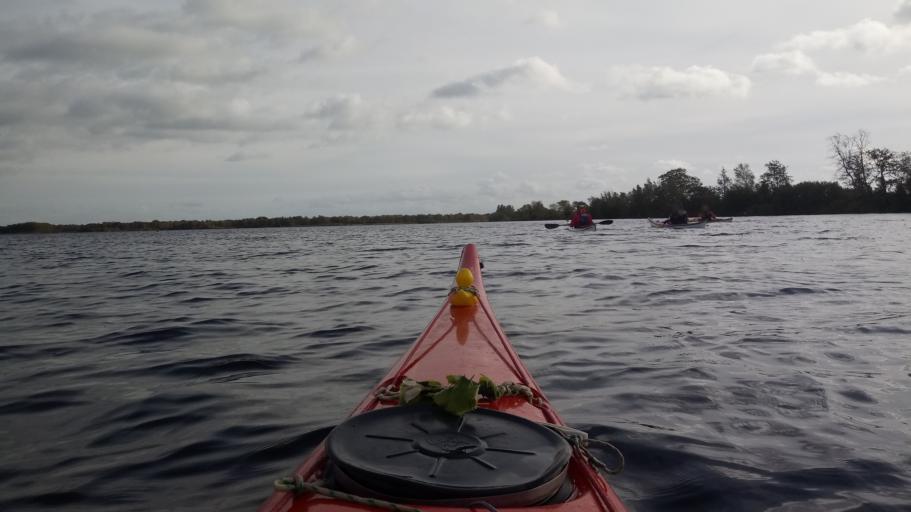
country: NL
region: Overijssel
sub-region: Gemeente Steenwijkerland
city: Wanneperveen
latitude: 52.6864
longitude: 6.0819
